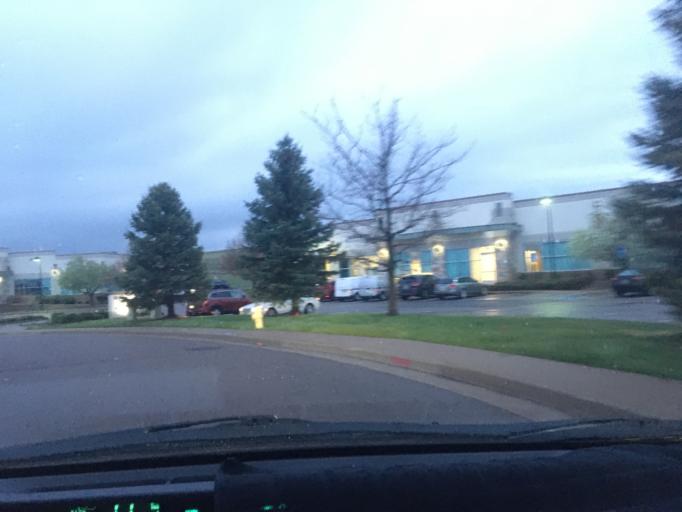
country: US
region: Colorado
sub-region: Broomfield County
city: Broomfield
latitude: 39.9037
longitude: -105.0990
